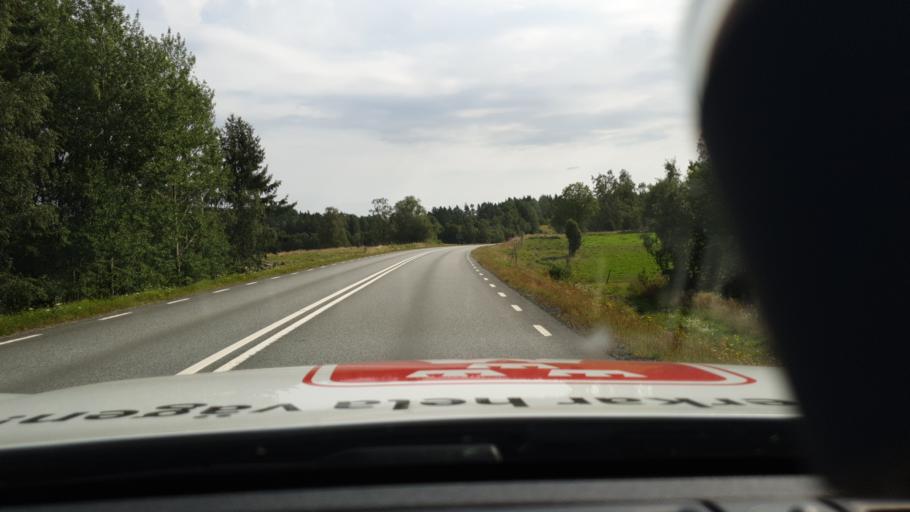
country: SE
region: Joenkoeping
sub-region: Aneby Kommun
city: Hestra
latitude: 57.7788
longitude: 14.5317
